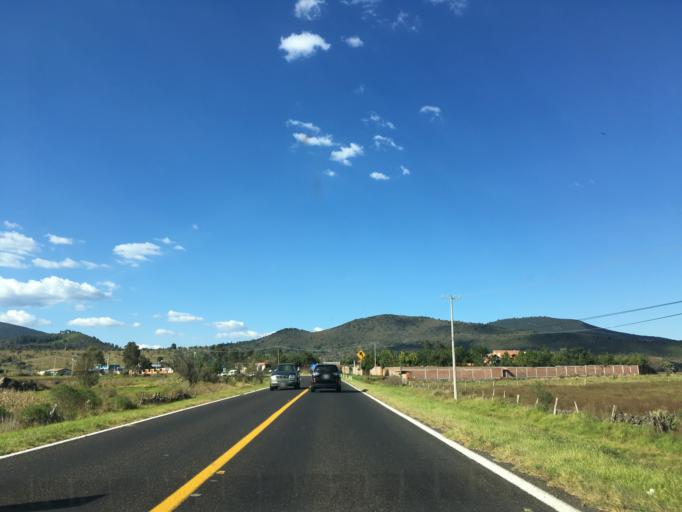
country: MX
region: Michoacan
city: Tzintzuntzan
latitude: 19.5684
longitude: -101.5718
